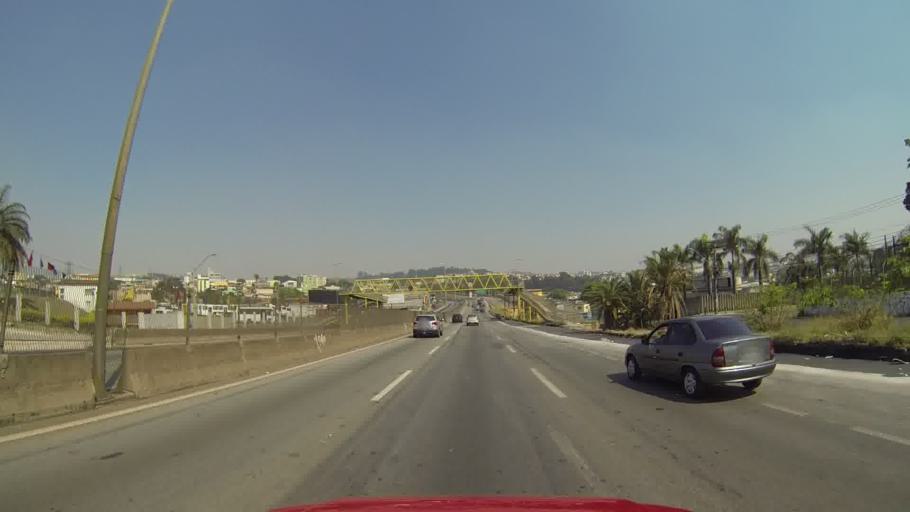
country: BR
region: Minas Gerais
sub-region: Contagem
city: Contagem
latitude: -19.9601
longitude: -44.0527
